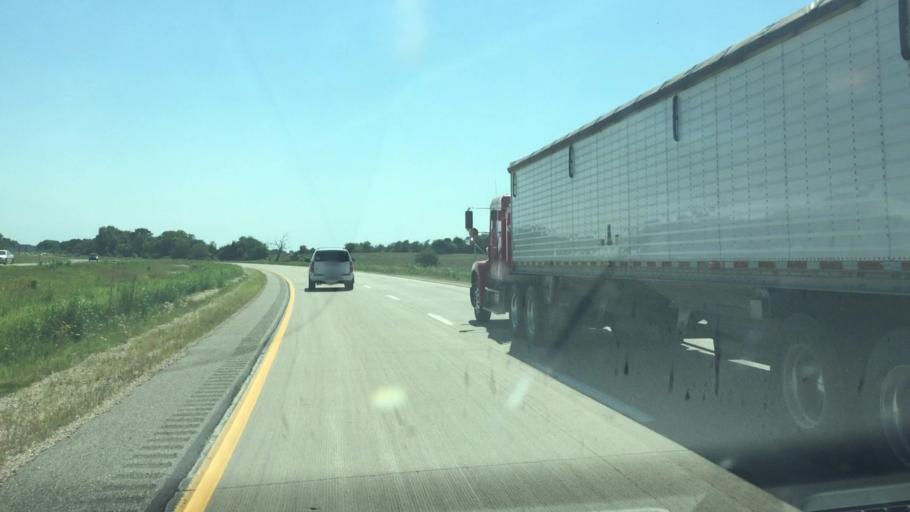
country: US
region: Iowa
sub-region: Jones County
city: Monticello
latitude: 42.2063
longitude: -91.1987
